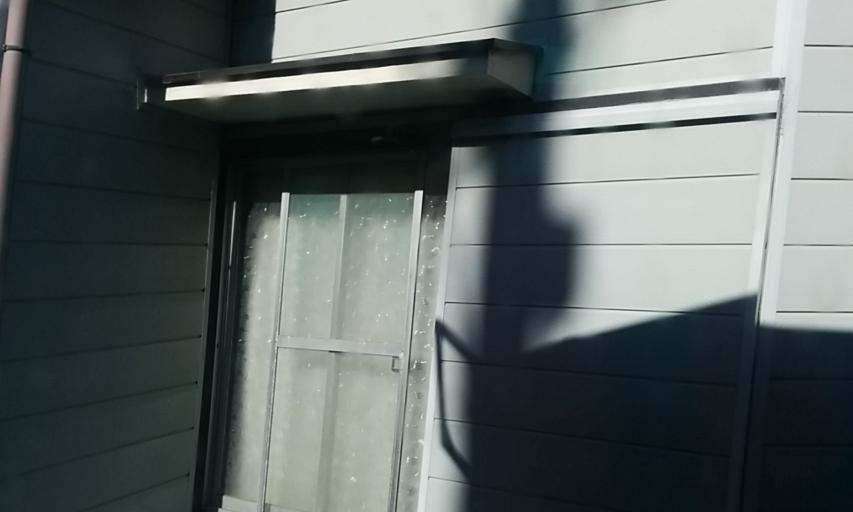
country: JP
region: Wakayama
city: Minato
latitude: 34.1907
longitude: 135.1470
